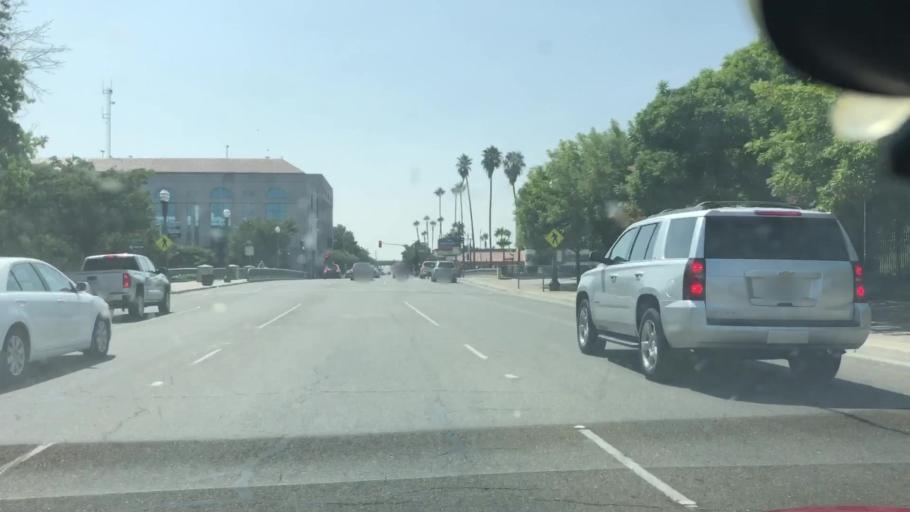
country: US
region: California
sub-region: San Joaquin County
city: Stockton
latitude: 37.9548
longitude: -121.2918
